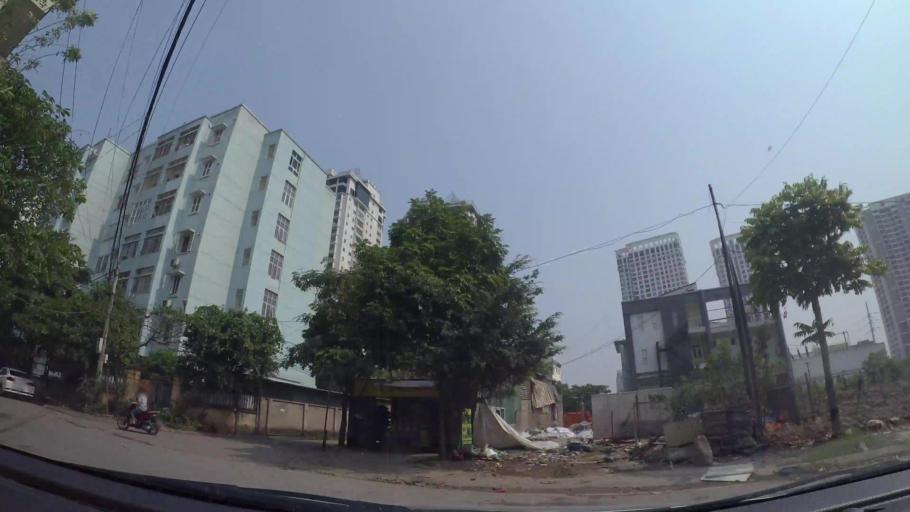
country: VN
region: Ha Noi
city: Tay Ho
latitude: 21.0867
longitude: 105.8121
